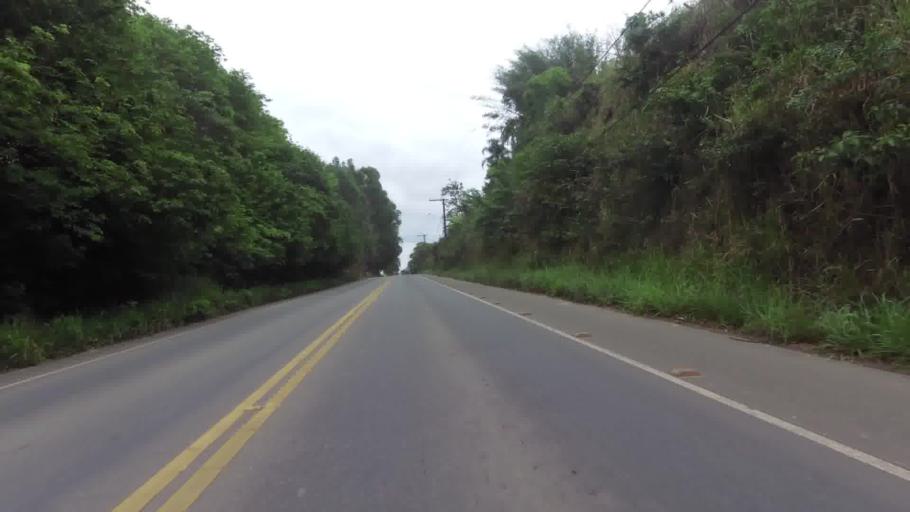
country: BR
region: Espirito Santo
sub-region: Piuma
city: Piuma
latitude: -20.8234
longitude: -40.7322
